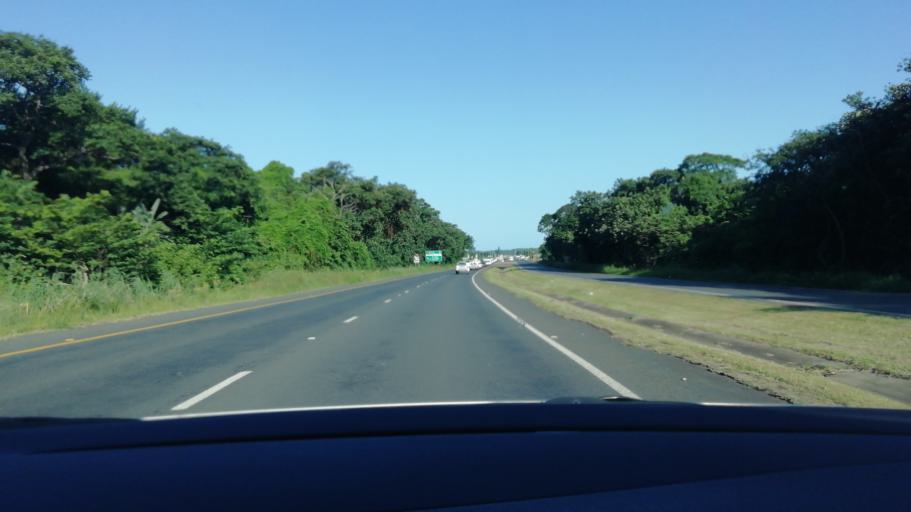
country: ZA
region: KwaZulu-Natal
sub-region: uThungulu District Municipality
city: Richards Bay
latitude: -28.7682
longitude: 32.0560
